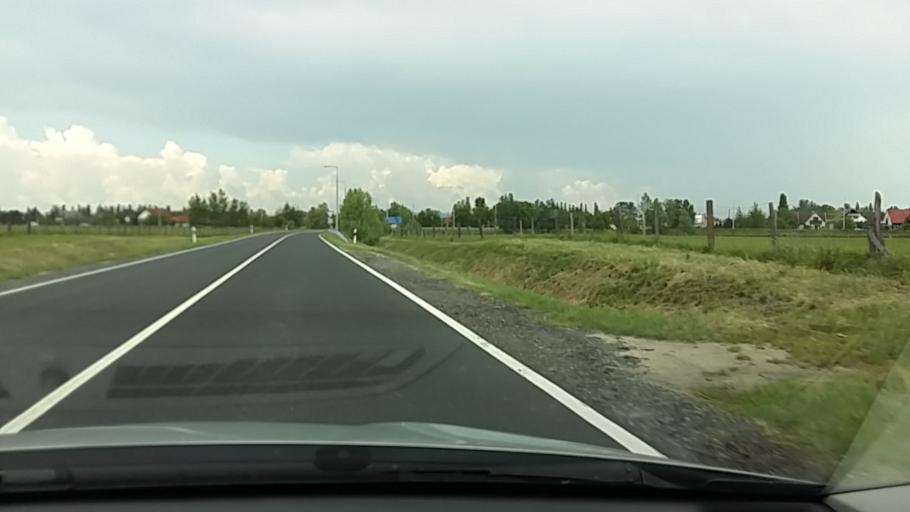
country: HU
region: Somogy
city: Balatonfenyves
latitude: 46.7041
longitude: 17.4689
